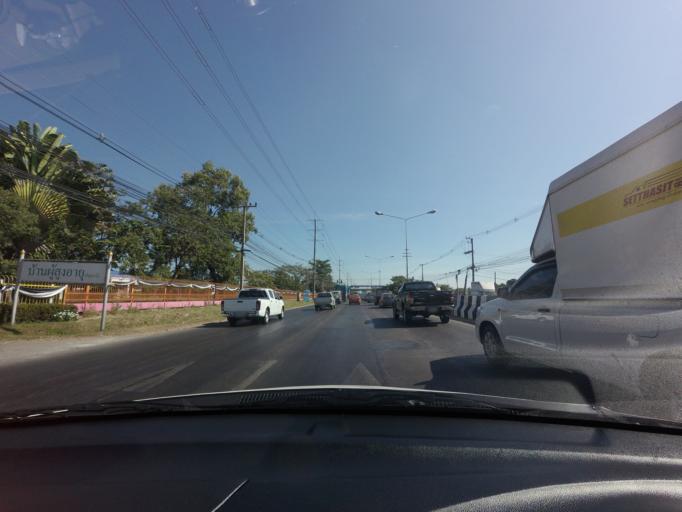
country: TH
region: Pathum Thani
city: Thanyaburi
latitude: 14.0127
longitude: 100.7164
